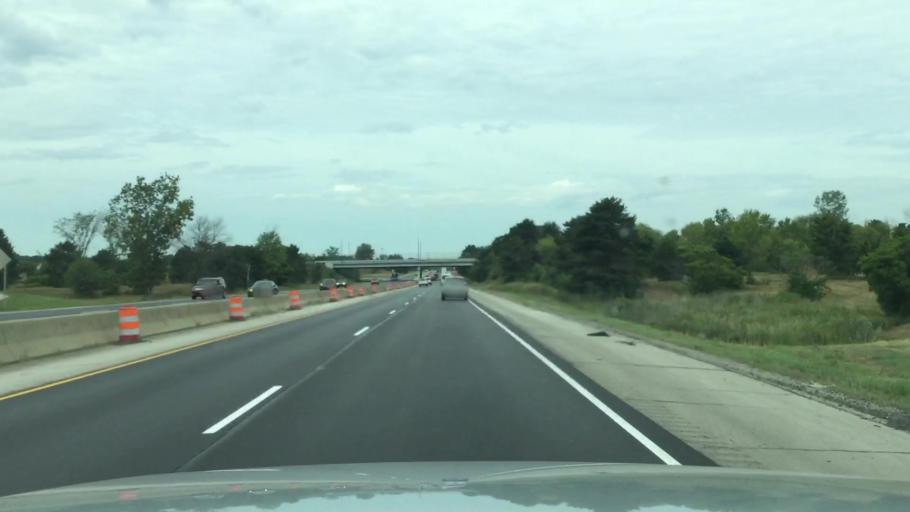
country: US
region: Michigan
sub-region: Washtenaw County
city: Ann Arbor
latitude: 42.2433
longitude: -83.7603
